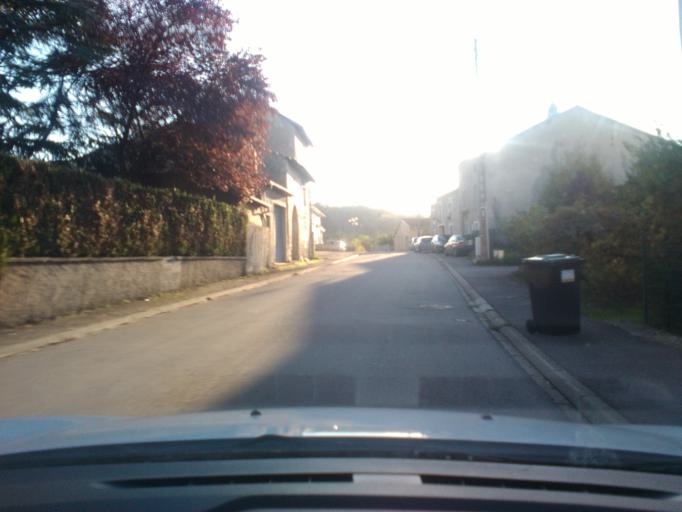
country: FR
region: Lorraine
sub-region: Departement des Vosges
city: Vincey
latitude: 48.3364
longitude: 6.3271
